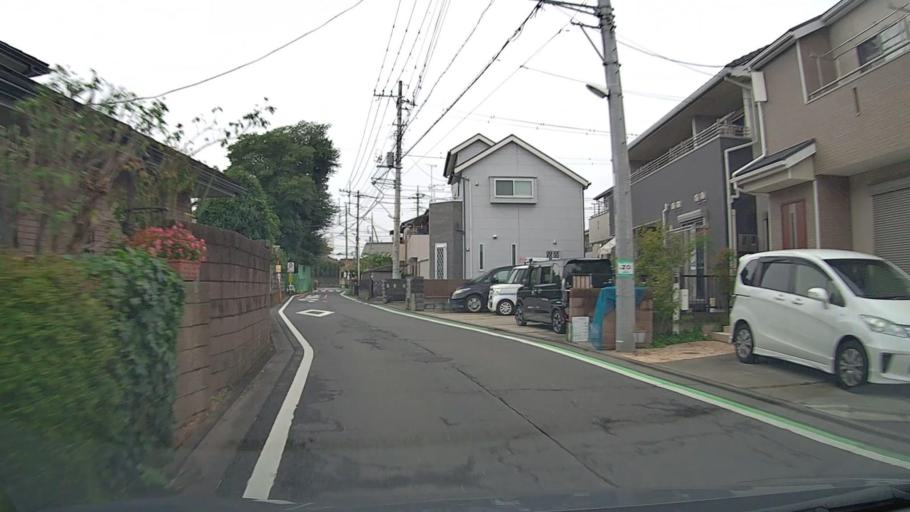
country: JP
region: Saitama
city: Tokorozawa
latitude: 35.7828
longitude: 139.4929
